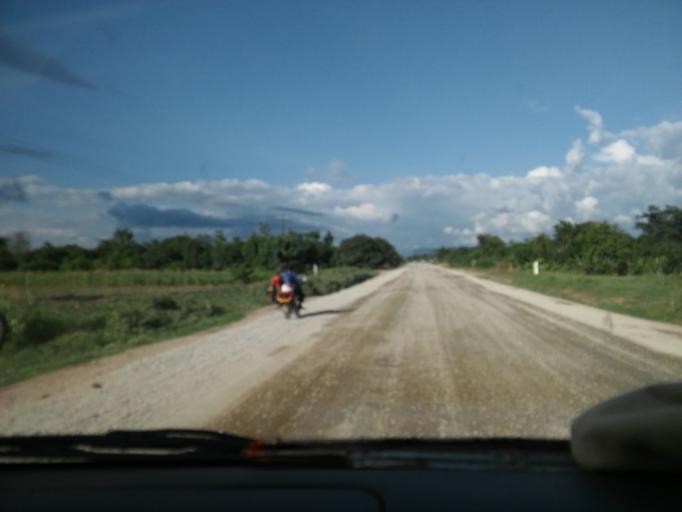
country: UG
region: Eastern Region
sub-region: Mbale District
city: Mbale
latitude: 1.0546
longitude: 34.0604
